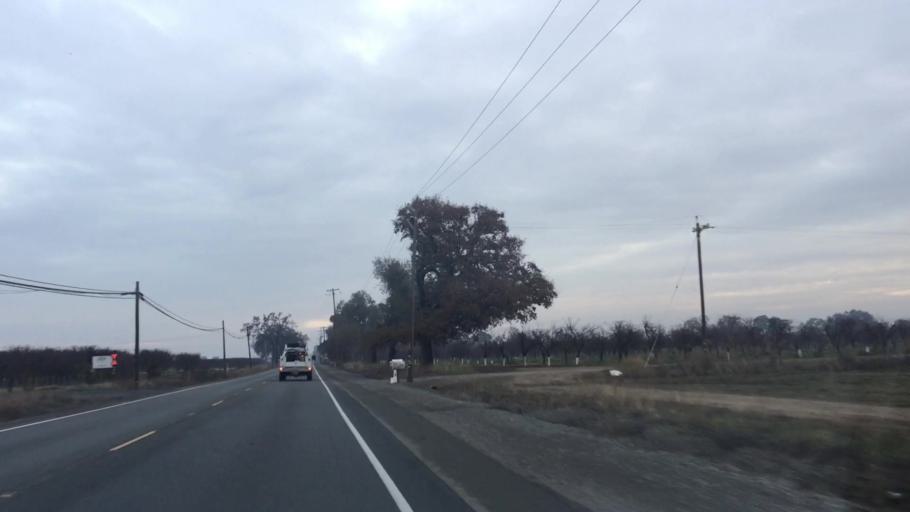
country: US
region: California
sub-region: Sutter County
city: Live Oak
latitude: 39.2598
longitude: -121.5981
